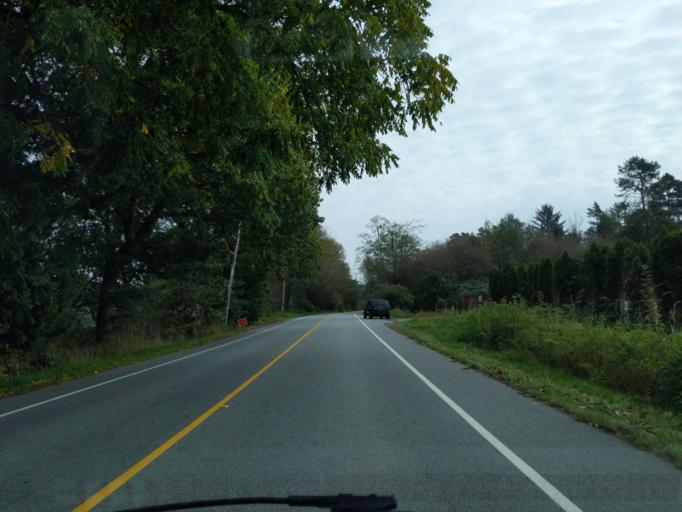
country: CA
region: British Columbia
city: Maple Ridge
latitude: 49.2059
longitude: -122.6060
